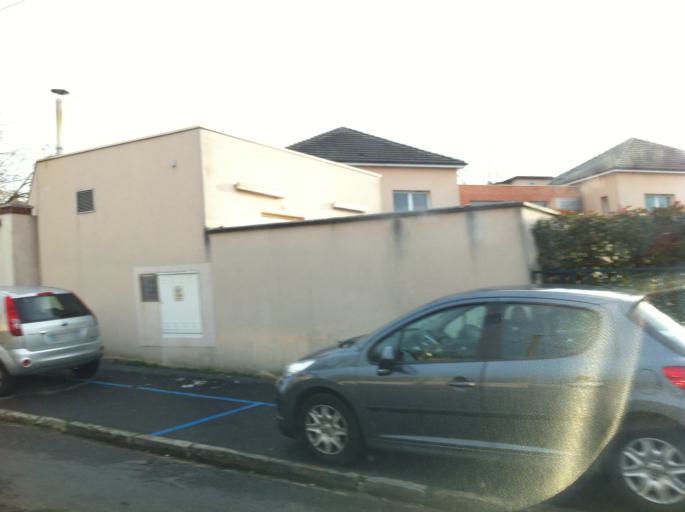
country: FR
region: Ile-de-France
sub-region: Departement de Seine-et-Marne
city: Dammarie-les-Lys
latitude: 48.5313
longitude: 2.6474
